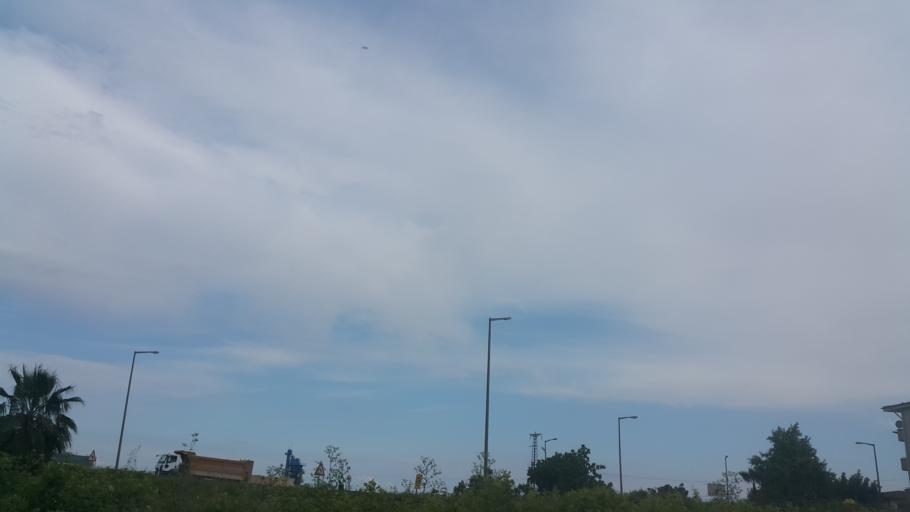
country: TR
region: Mersin
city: Yenice
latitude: 36.9503
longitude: 34.9919
